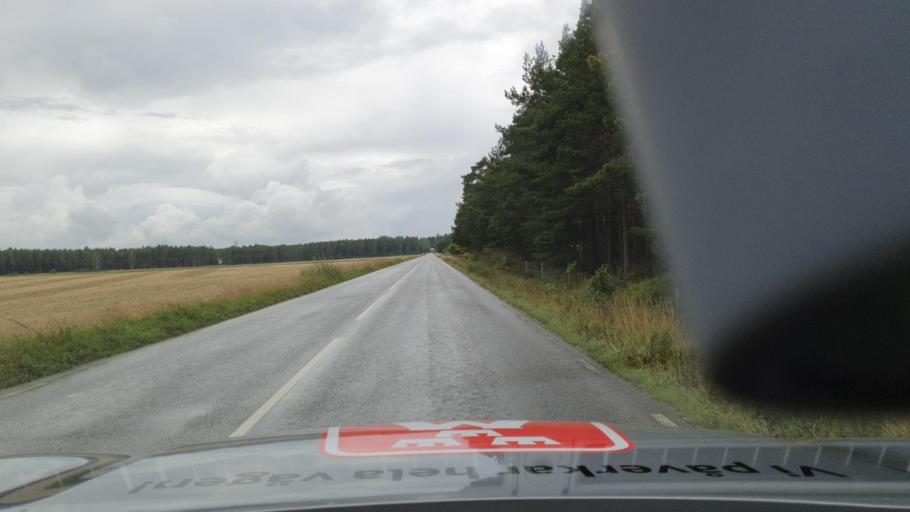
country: SE
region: Gotland
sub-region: Gotland
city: Visby
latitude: 57.4979
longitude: 18.3820
